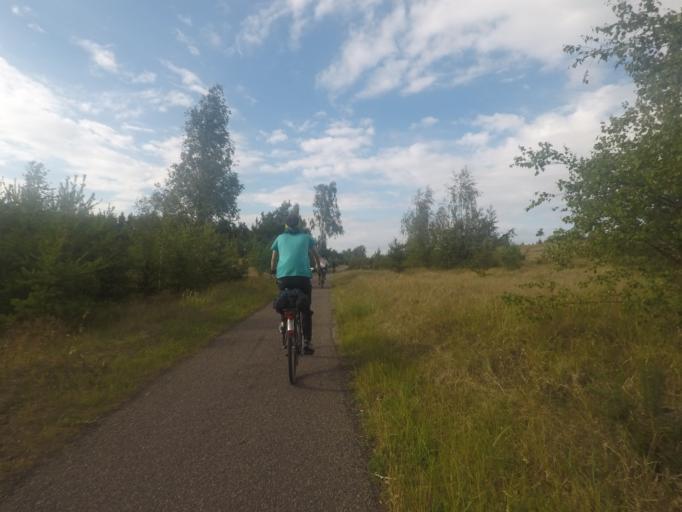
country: LT
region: Klaipedos apskritis
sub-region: Klaipeda
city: Klaipeda
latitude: 55.6336
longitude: 21.1163
